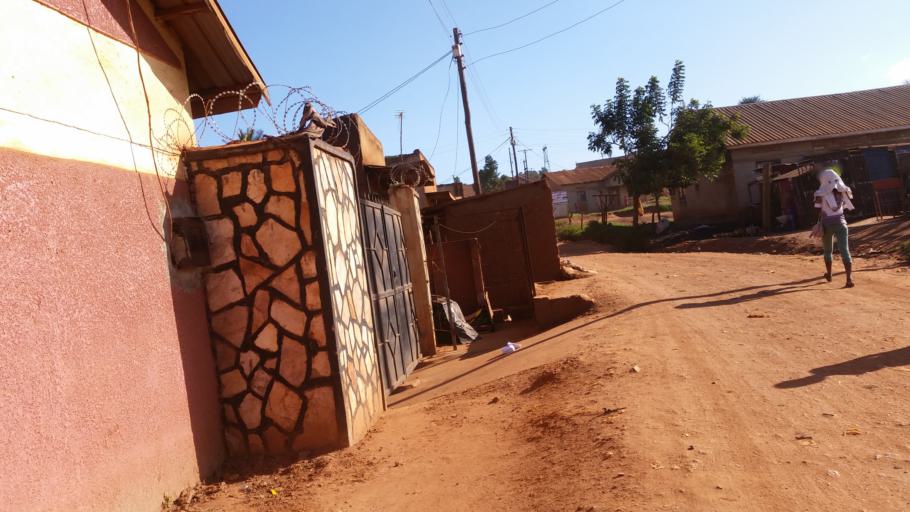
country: UG
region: Central Region
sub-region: Wakiso District
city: Kireka
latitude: 0.3249
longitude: 32.6459
